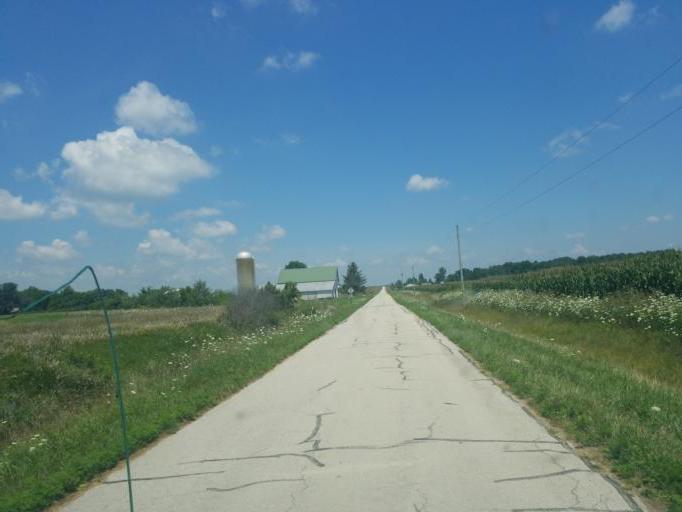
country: US
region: Ohio
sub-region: Allen County
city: Spencerville
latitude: 40.6669
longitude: -84.4351
